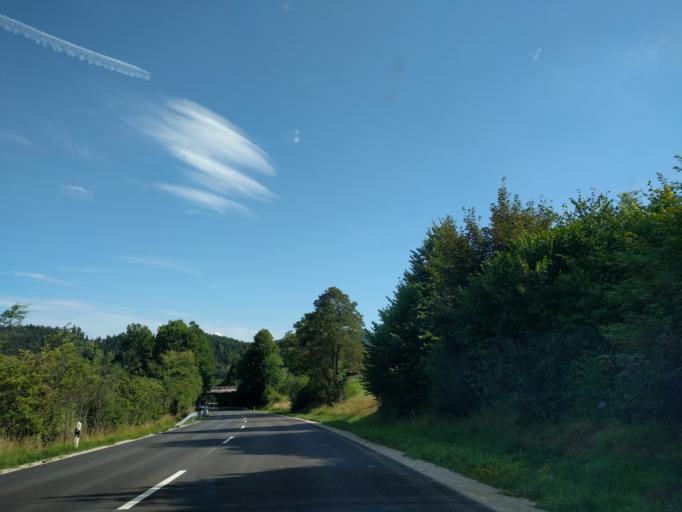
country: DE
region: Bavaria
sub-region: Lower Bavaria
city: Regen
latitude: 48.9784
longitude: 13.1356
